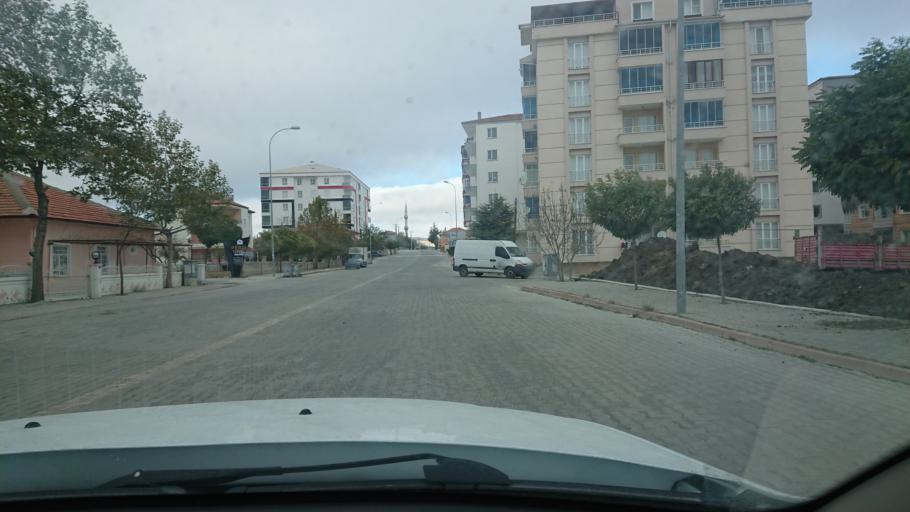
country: TR
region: Aksaray
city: Ortakoy
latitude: 38.7411
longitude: 34.0348
